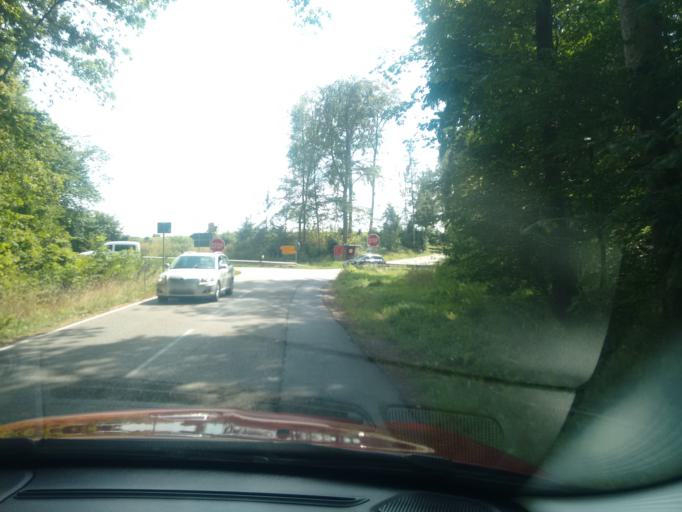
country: DE
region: Bavaria
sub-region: Upper Bavaria
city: Tacherting
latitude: 48.0535
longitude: 12.5923
